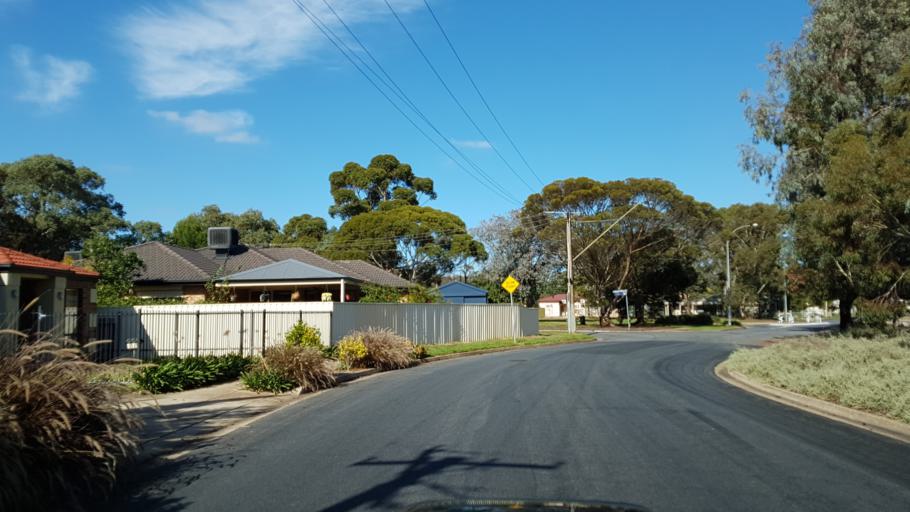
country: AU
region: South Australia
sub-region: Salisbury
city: Salisbury
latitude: -34.7531
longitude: 138.6373
